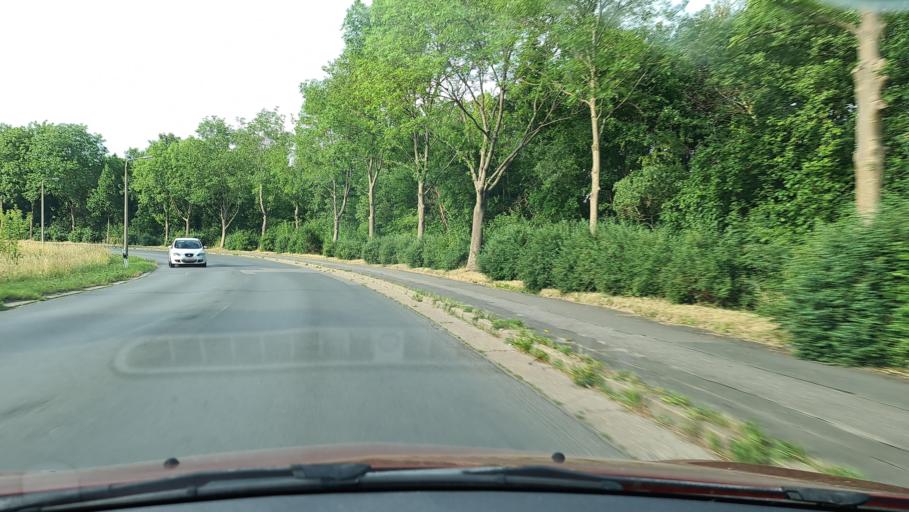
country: DE
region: Saxony
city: Lichtentanne
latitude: 50.7033
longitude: 12.4627
